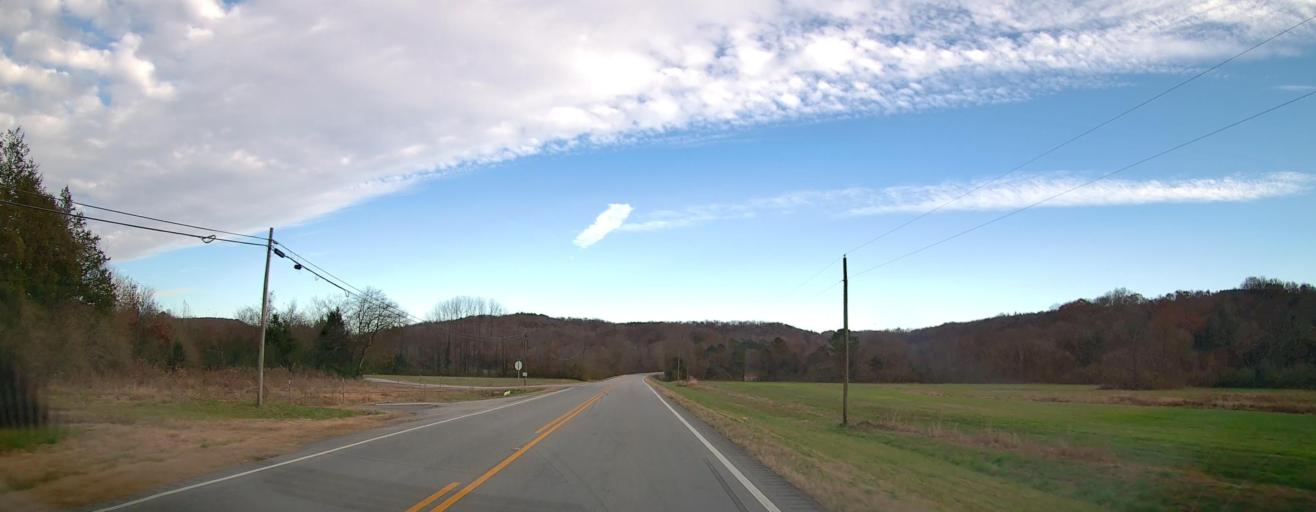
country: US
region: Alabama
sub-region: Marshall County
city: Arab
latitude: 34.3711
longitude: -86.6443
